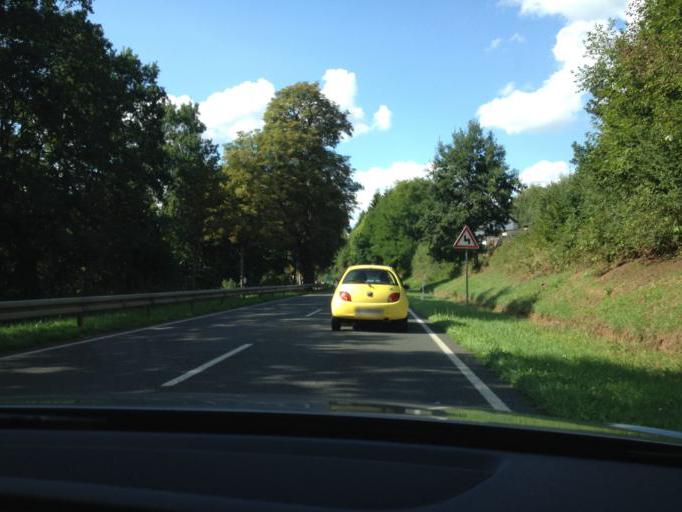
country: DE
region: Saarland
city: Illingen
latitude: 49.4058
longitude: 7.0205
